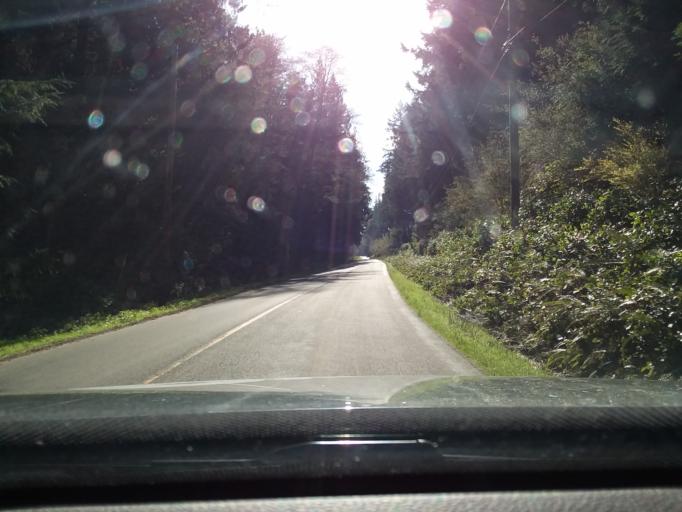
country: CA
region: British Columbia
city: North Cowichan
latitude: 48.9341
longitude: -123.4767
